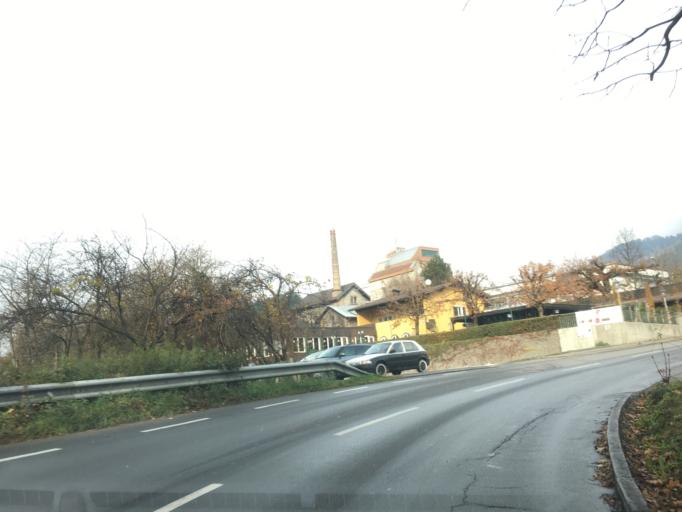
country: AT
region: Vorarlberg
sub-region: Politischer Bezirk Bludenz
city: Bludenz
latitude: 47.1569
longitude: 9.8141
